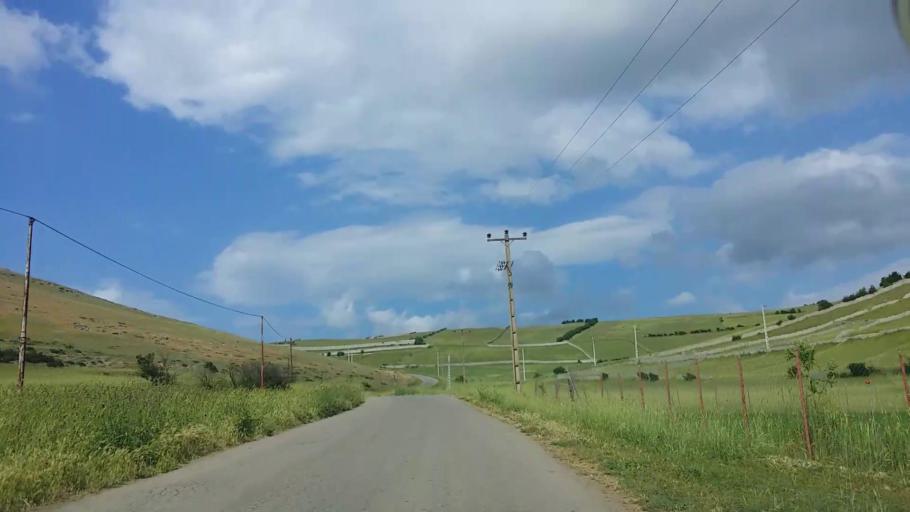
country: IR
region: Mazandaran
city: Chalus
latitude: 36.5254
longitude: 51.2648
